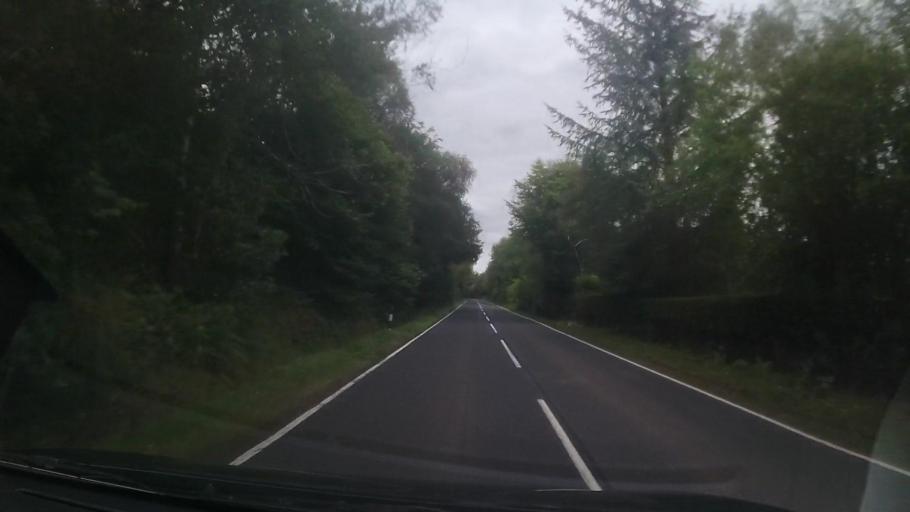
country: GB
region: Scotland
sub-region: Argyll and Bute
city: Garelochhead
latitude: 56.2040
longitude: -5.0601
